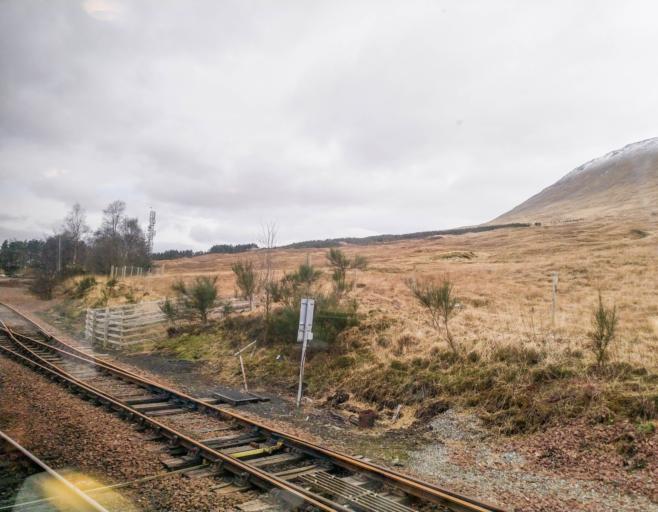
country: GB
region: Scotland
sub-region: Highland
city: Spean Bridge
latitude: 56.5149
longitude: -4.7633
